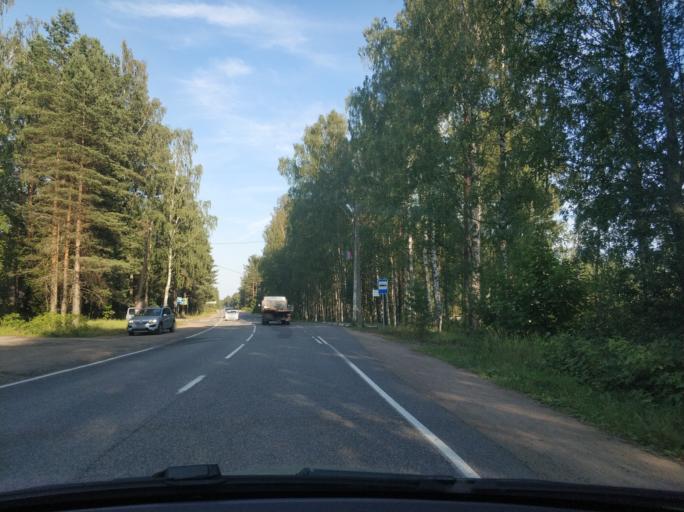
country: RU
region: Leningrad
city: Borisova Griva
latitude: 60.0930
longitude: 30.9841
